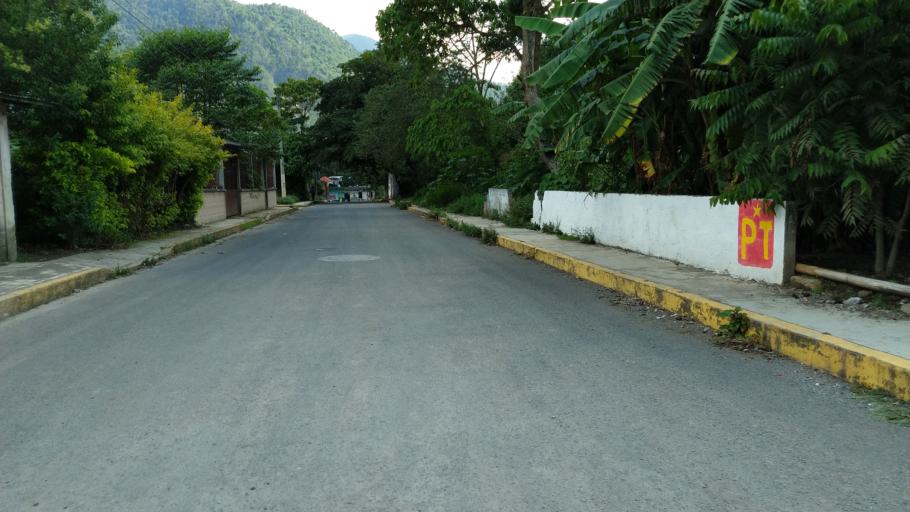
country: MX
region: Veracruz
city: Jalapilla
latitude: 18.8133
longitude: -97.0687
